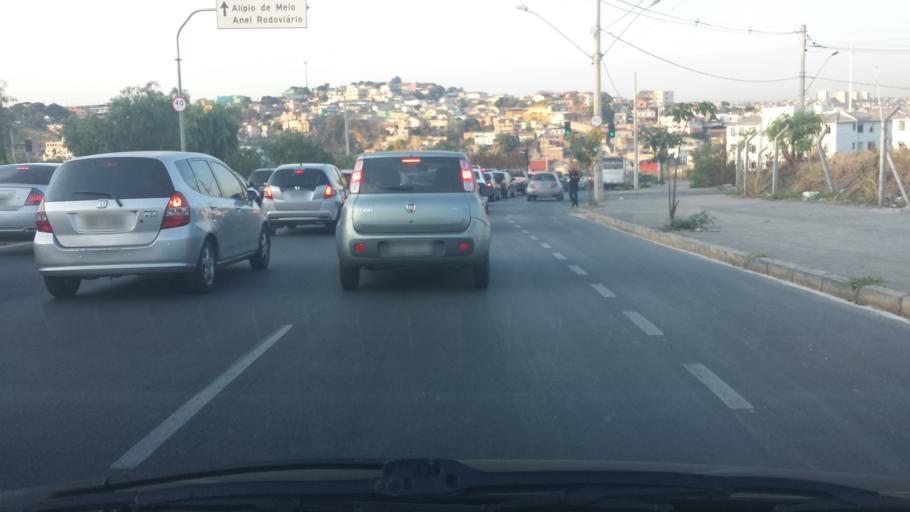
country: BR
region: Minas Gerais
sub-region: Belo Horizonte
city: Belo Horizonte
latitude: -19.8986
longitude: -43.9925
